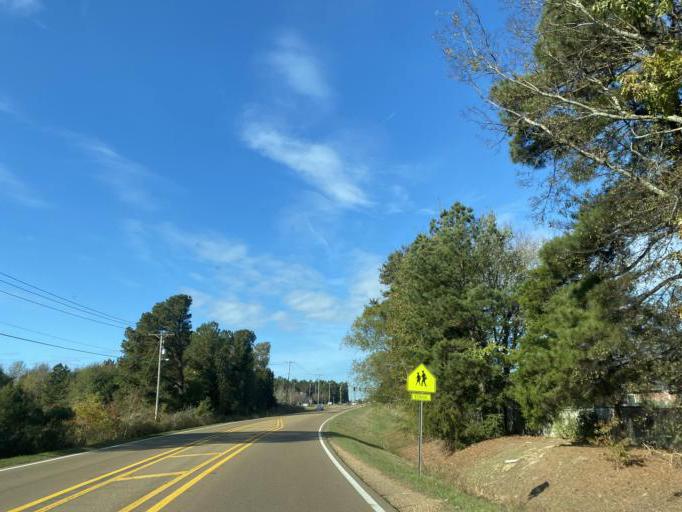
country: US
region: Mississippi
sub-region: Madison County
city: Madison
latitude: 32.4805
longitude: -90.1644
